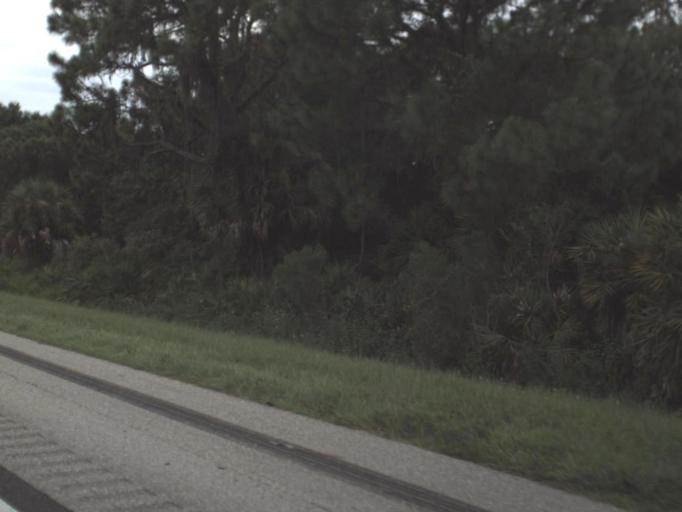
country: US
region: Florida
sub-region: Sarasota County
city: Vamo
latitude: 27.2340
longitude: -82.4529
